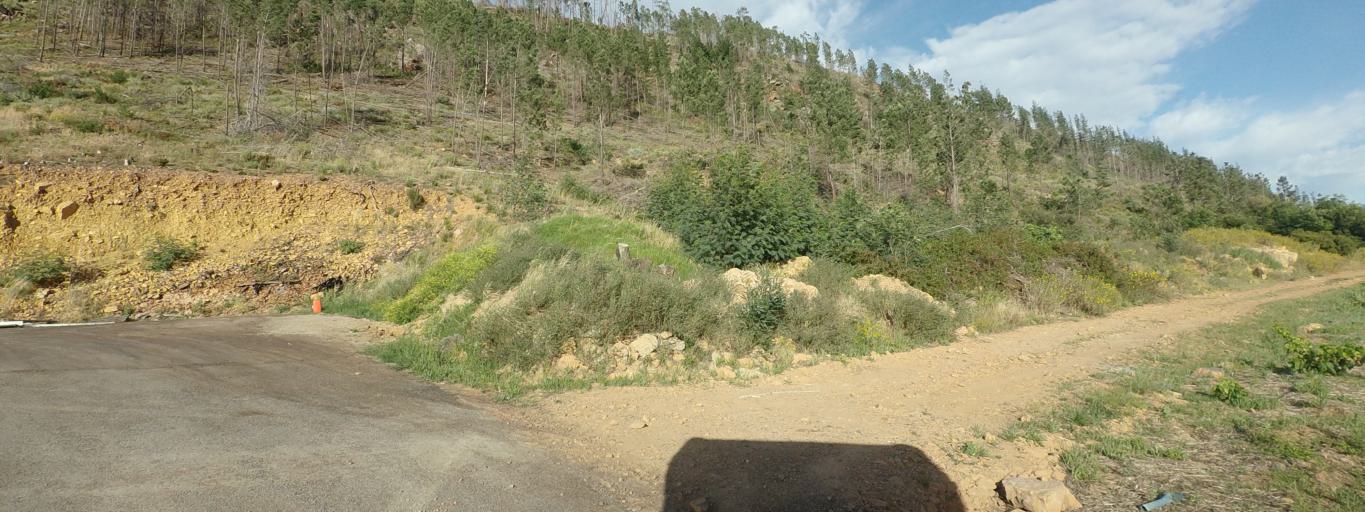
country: ZA
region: Western Cape
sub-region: Cape Winelands District Municipality
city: Paarl
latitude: -33.8979
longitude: 19.0906
